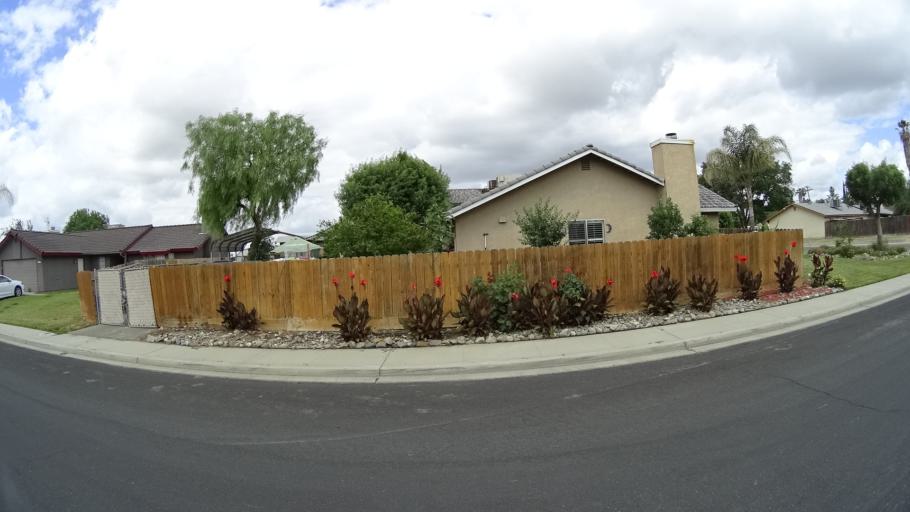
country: US
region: California
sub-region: Kings County
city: Hanford
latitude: 36.3307
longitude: -119.6274
